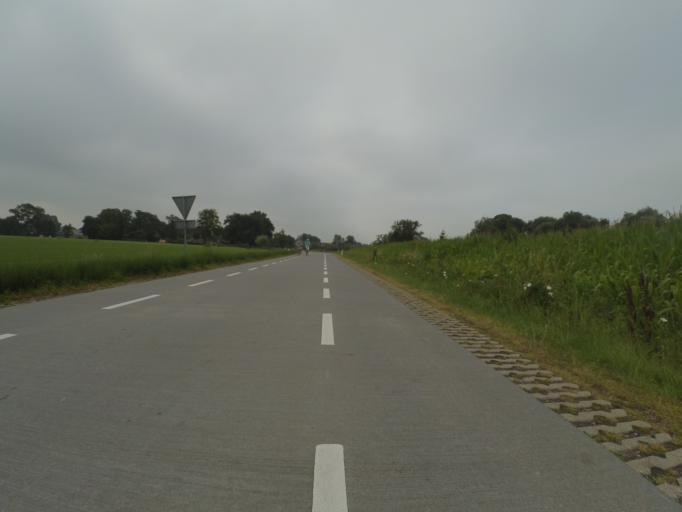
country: NL
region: Gelderland
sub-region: Gemeente Barneveld
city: Barneveld
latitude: 52.1198
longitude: 5.5765
